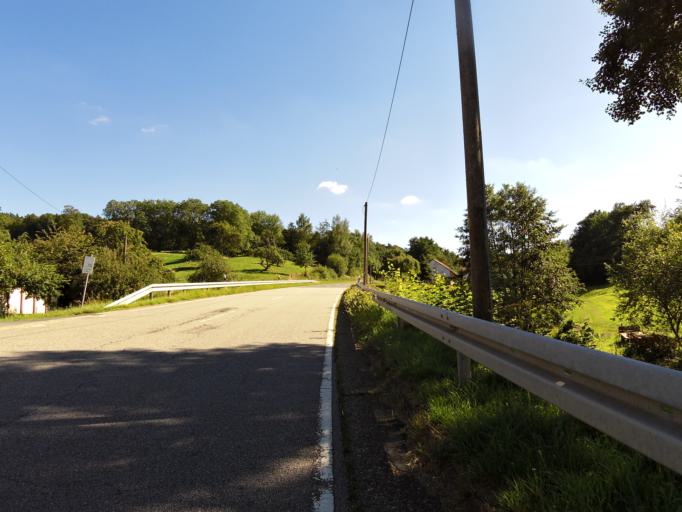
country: DE
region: Hesse
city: Reichelsheim
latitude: 49.6715
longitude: 8.8683
